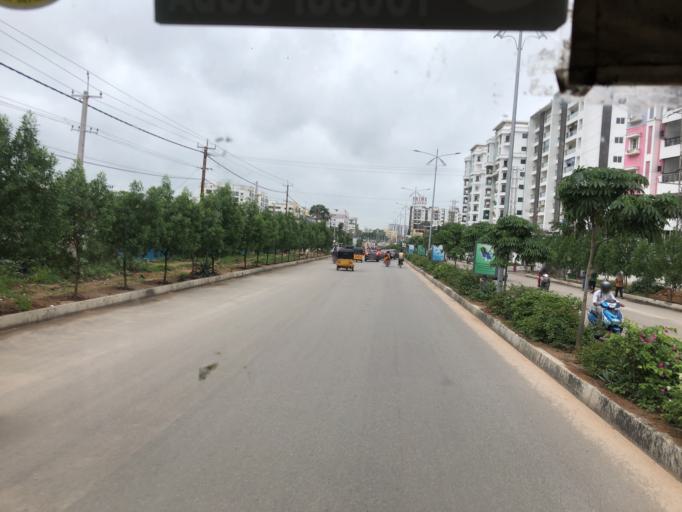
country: IN
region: Telangana
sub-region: Medak
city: Serilingampalle
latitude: 17.4622
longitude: 78.3508
